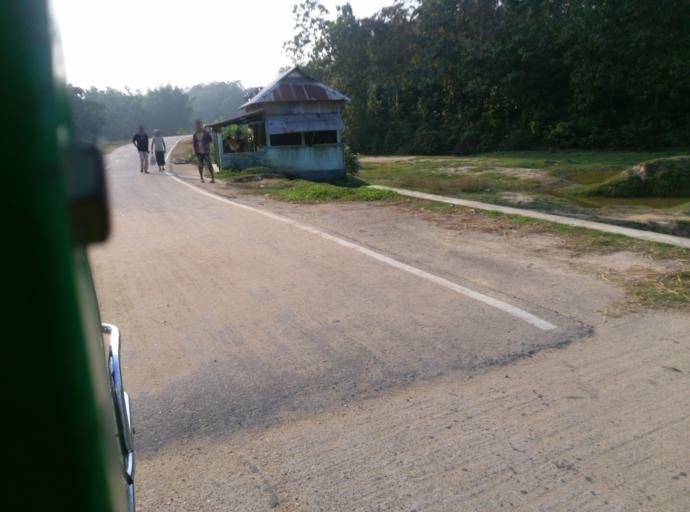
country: BD
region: Dhaka
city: Netrakona
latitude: 25.1731
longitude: 90.6456
